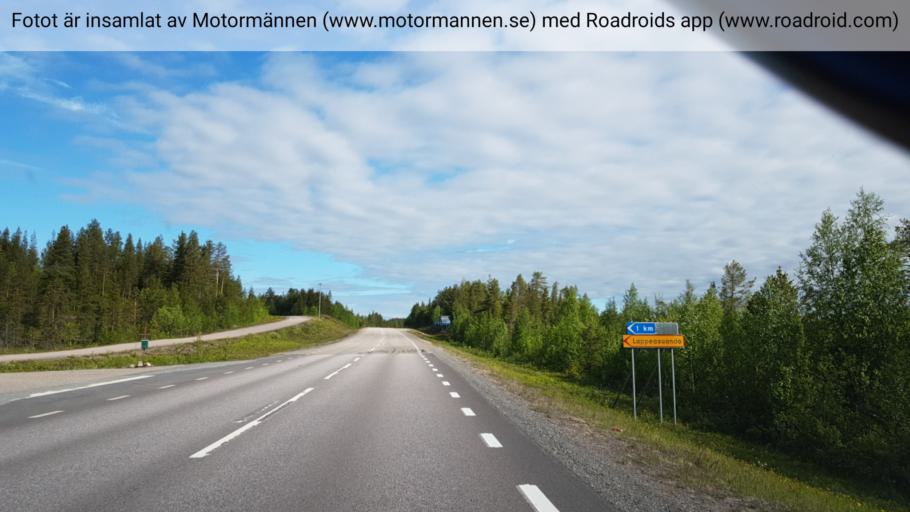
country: SE
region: Norrbotten
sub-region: Gallivare Kommun
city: Malmberget
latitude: 67.4775
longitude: 21.1275
